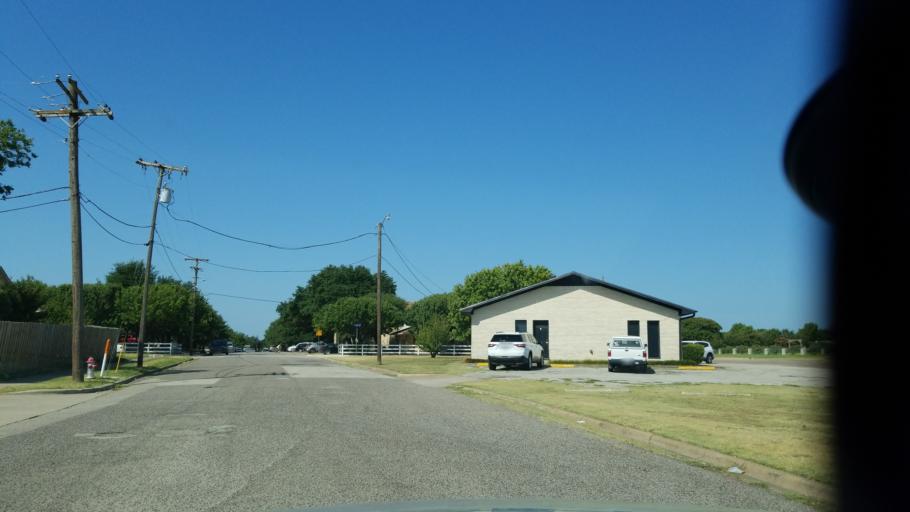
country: US
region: Texas
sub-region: Dallas County
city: Duncanville
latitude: 32.6472
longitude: -96.9021
